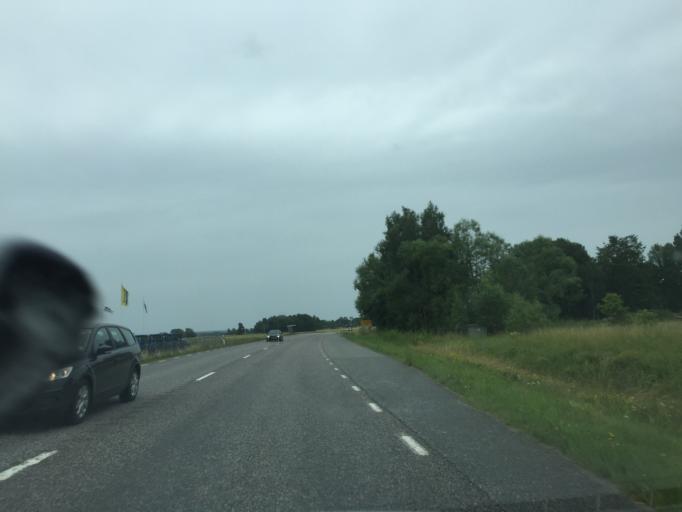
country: SE
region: OErebro
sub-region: Kumla Kommun
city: Hallabrottet
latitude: 59.1771
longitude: 15.2600
